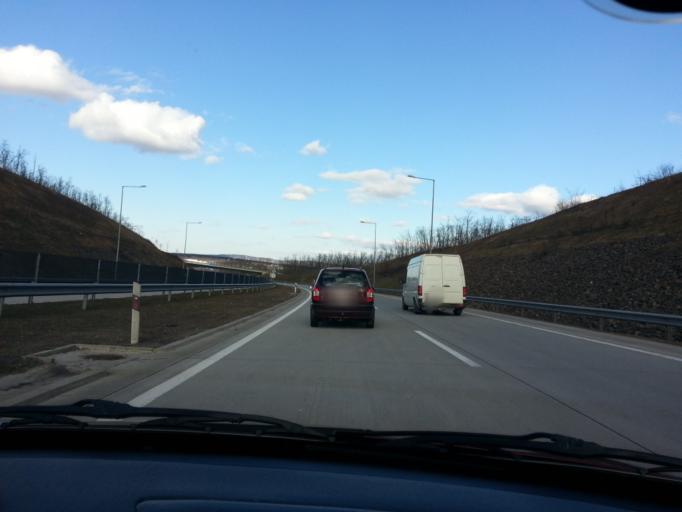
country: HU
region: Pest
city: Godollo
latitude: 47.5700
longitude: 19.3269
